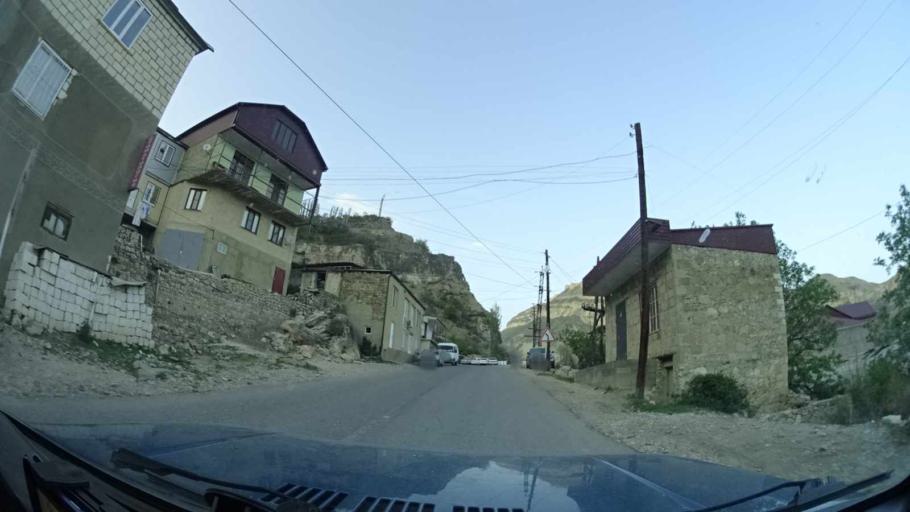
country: RU
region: Dagestan
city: Gunib
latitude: 42.3834
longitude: 46.9629
